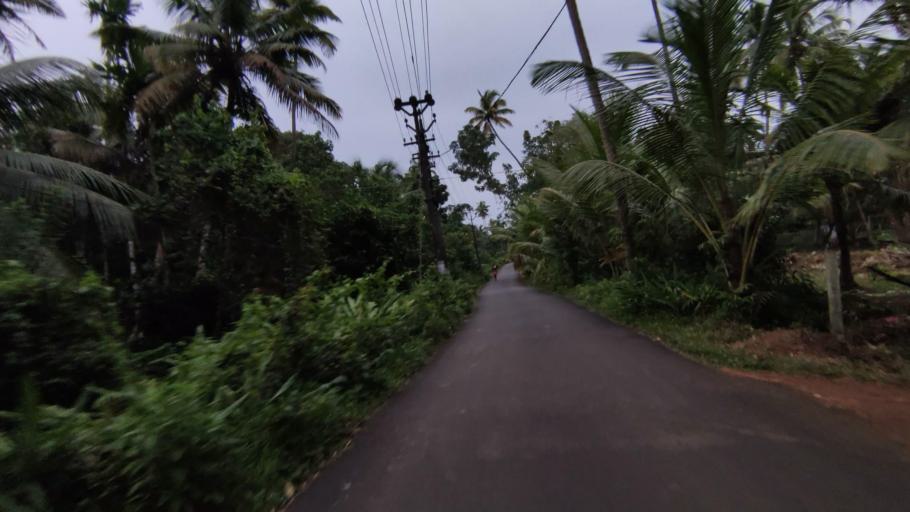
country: IN
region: Kerala
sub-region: Alappuzha
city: Shertallai
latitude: 9.6720
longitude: 76.3695
